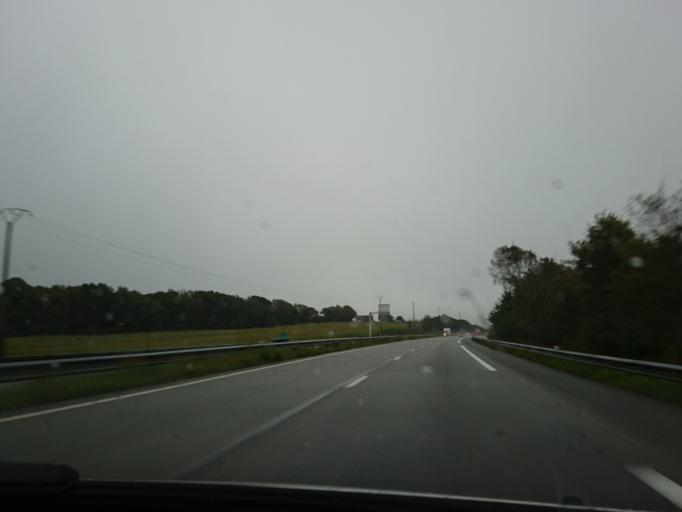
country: FR
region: Brittany
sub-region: Departement du Finistere
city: Briec
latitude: 48.1214
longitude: -4.0227
